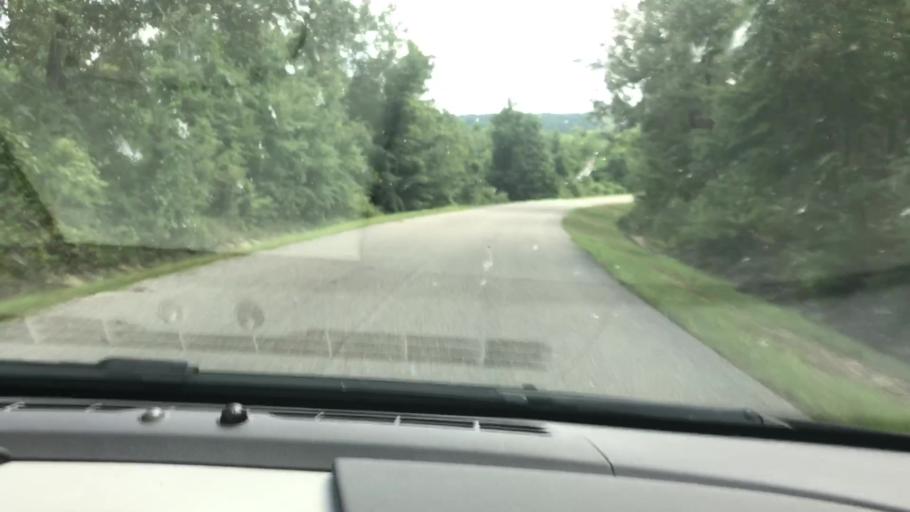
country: US
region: Georgia
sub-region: Clay County
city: Fort Gaines
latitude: 31.7408
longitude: -85.0753
